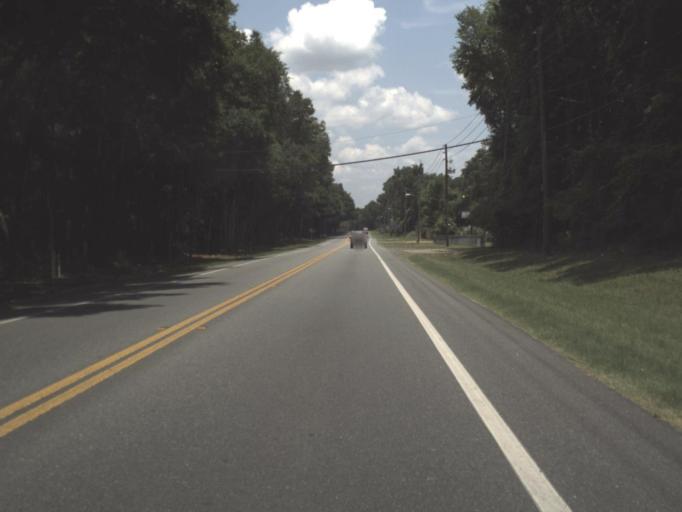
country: US
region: Florida
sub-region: Alachua County
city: Newberry
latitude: 29.6460
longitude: -82.6275
